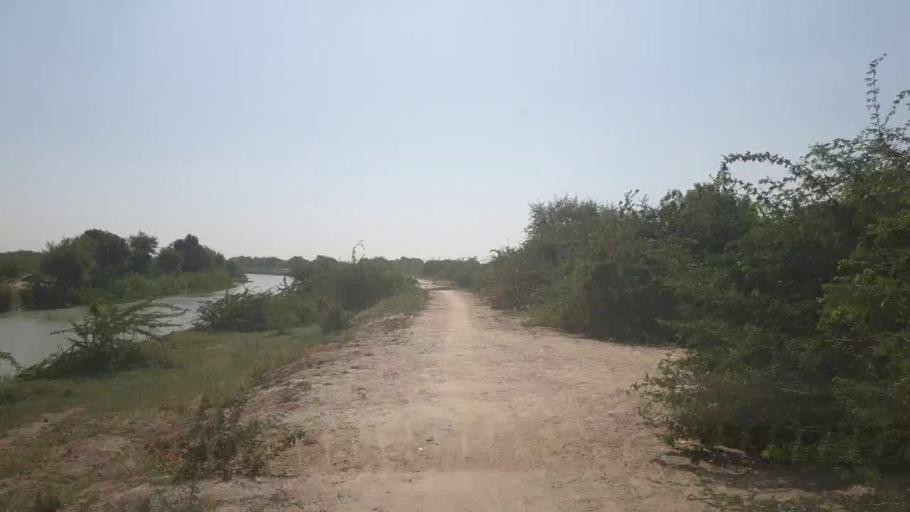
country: PK
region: Sindh
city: Talhar
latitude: 24.8048
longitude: 68.7921
